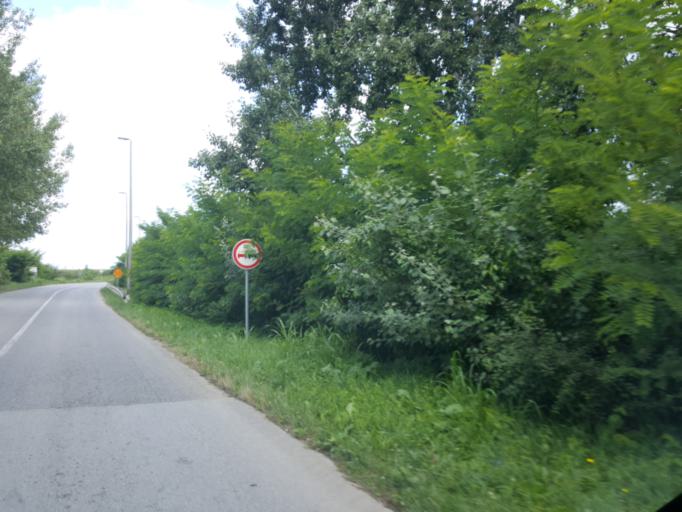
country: RS
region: Autonomna Pokrajina Vojvodina
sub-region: Sremski Okrug
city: Sid
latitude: 45.0431
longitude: 19.2141
